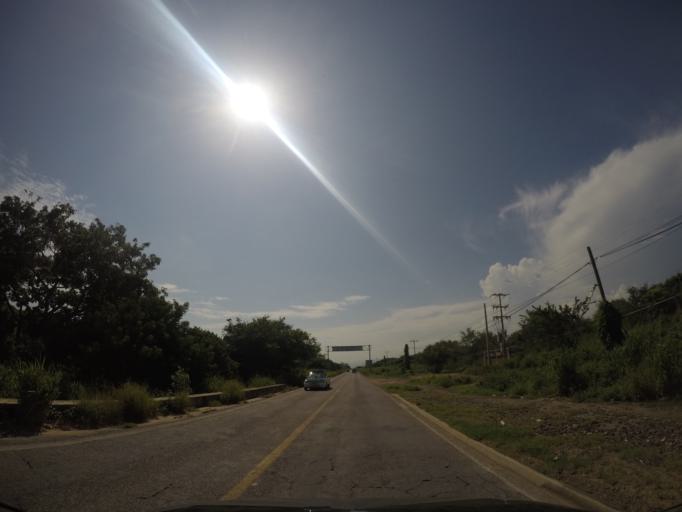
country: MX
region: Oaxaca
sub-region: San Pedro Mixtepec -Dto. 22 -
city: Puerto Escondido
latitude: 15.8731
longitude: -97.0949
